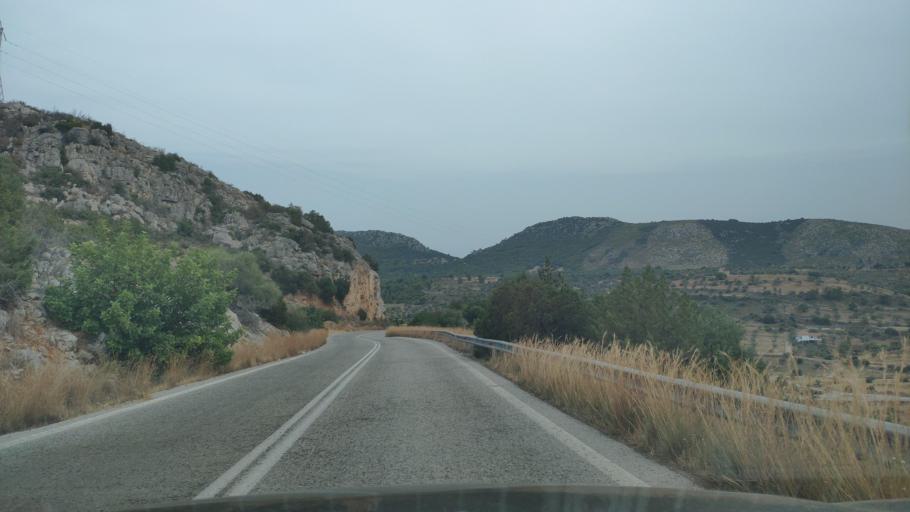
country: GR
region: Peloponnese
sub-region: Nomos Argolidos
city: Didyma
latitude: 37.4379
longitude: 23.1849
